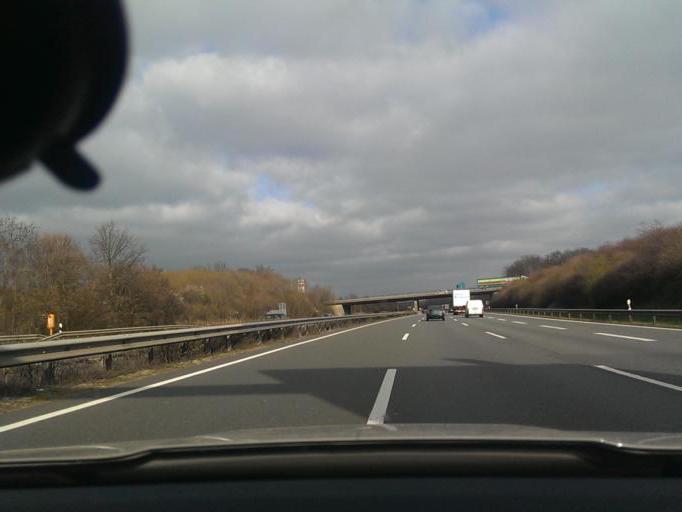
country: DE
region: North Rhine-Westphalia
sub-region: Regierungsbezirk Detmold
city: Vlotho
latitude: 52.2113
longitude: 8.8719
